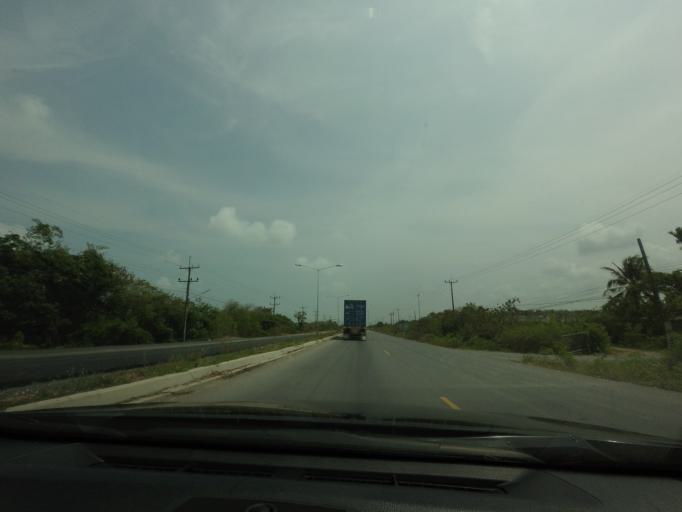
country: TH
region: Songkhla
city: Ranot
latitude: 7.9112
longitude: 100.3379
